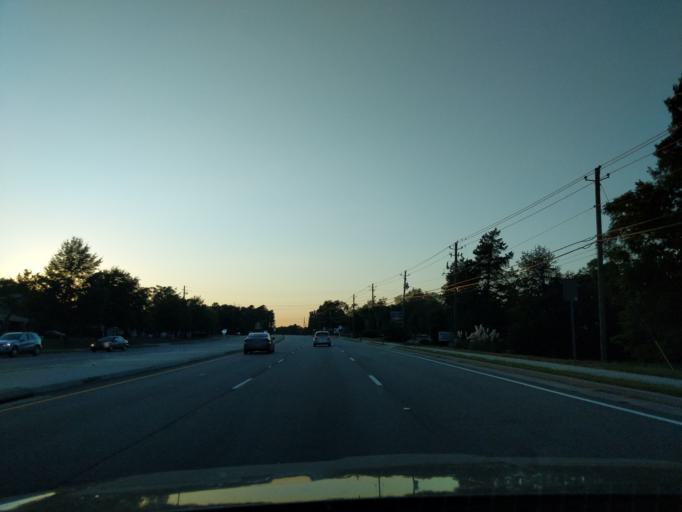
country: US
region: Georgia
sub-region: Columbia County
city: Martinez
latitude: 33.5185
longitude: -82.0785
